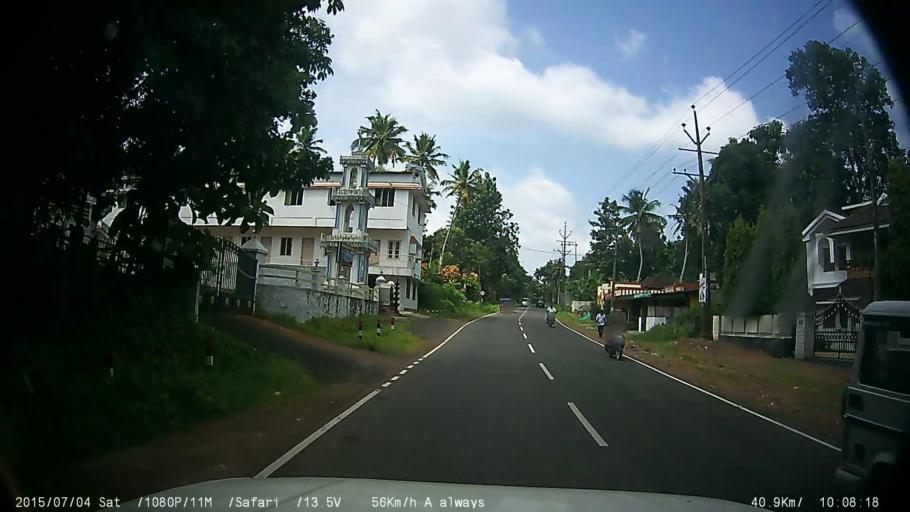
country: IN
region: Kerala
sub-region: Kottayam
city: Changanacheri
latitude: 9.4949
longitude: 76.5733
